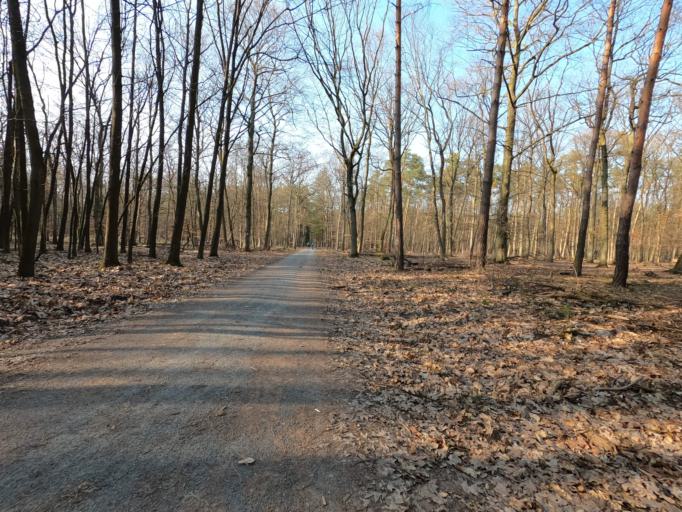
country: DE
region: Hesse
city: Raunheim
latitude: 50.0064
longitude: 8.5066
